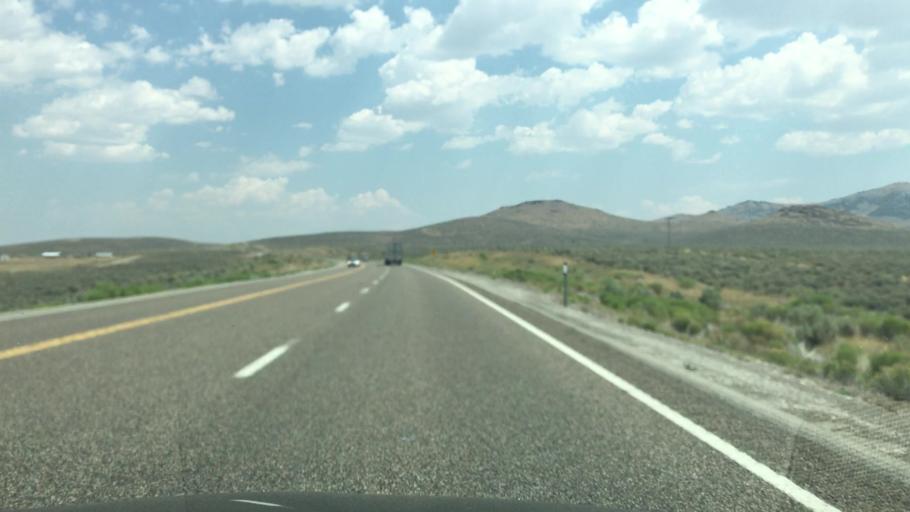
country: US
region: Nevada
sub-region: Elko County
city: Wells
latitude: 41.1716
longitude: -114.8821
